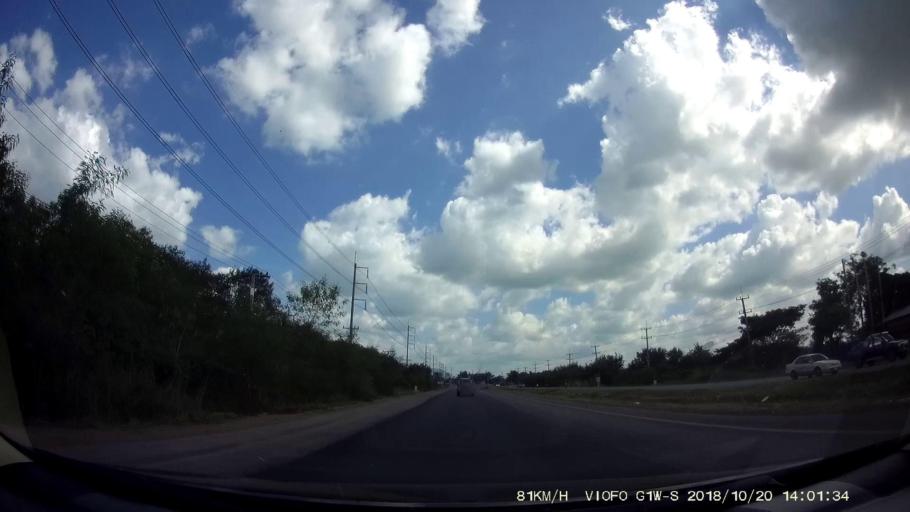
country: TH
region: Khon Kaen
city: Chum Phae
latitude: 16.5009
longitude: 102.1216
